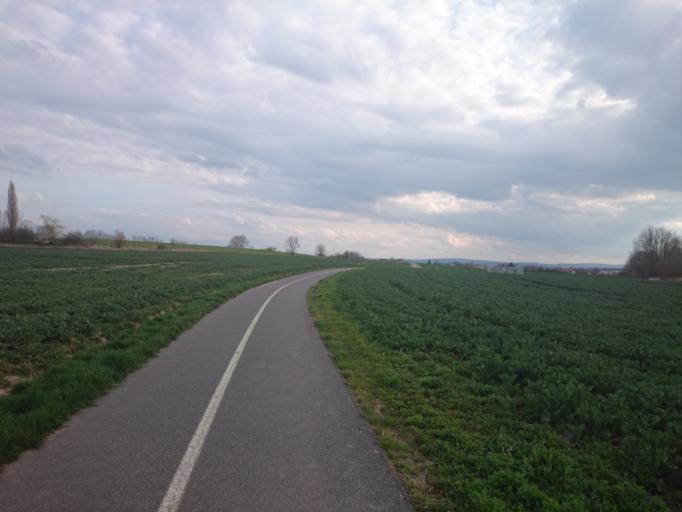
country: CZ
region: Pardubicky
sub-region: Okres Pardubice
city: Pardubice
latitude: 50.0100
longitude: 15.7631
